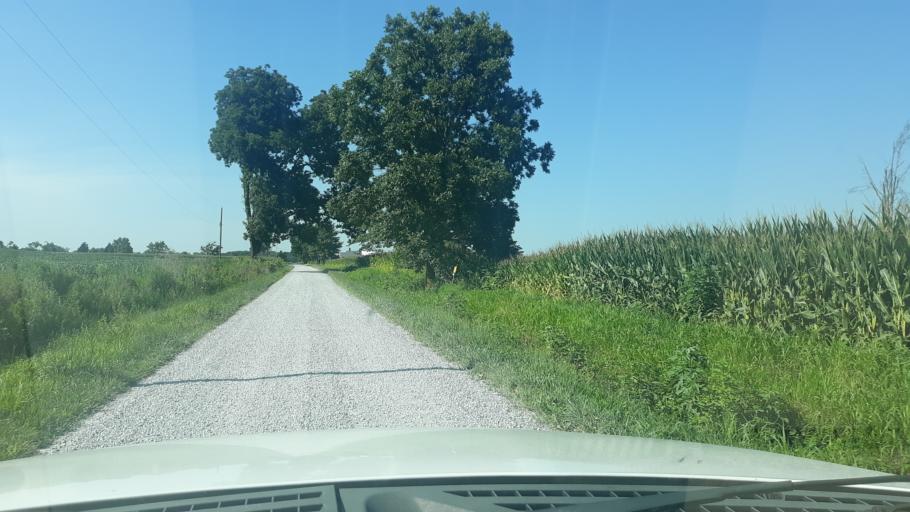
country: US
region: Illinois
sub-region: Saline County
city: Eldorado
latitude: 37.8609
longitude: -88.4850
